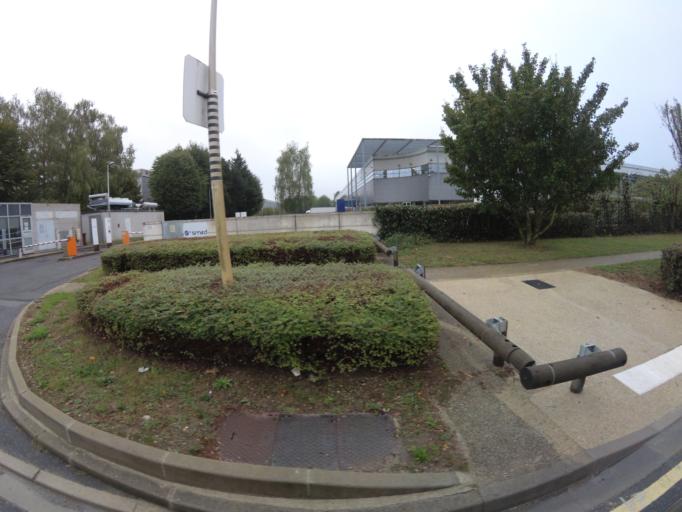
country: FR
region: Ile-de-France
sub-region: Departement de Seine-et-Marne
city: Ferrieres-en-Brie
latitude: 48.8319
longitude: 2.7174
